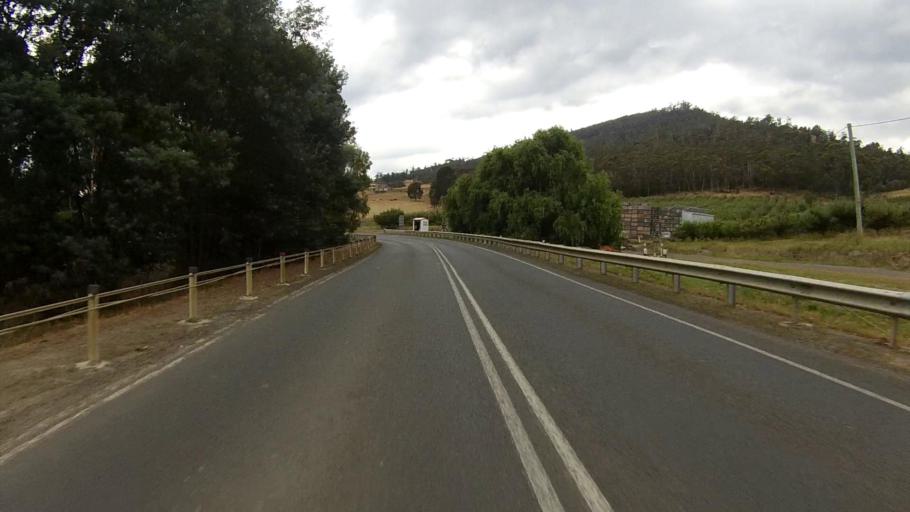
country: AU
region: Tasmania
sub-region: Huon Valley
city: Franklin
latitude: -43.0888
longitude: 147.0284
